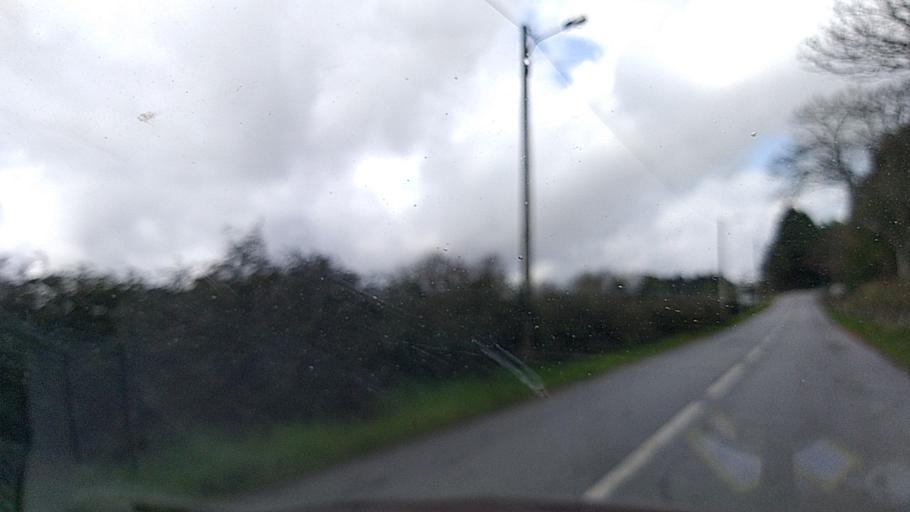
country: PT
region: Guarda
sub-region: Fornos de Algodres
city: Fornos de Algodres
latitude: 40.6314
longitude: -7.5423
